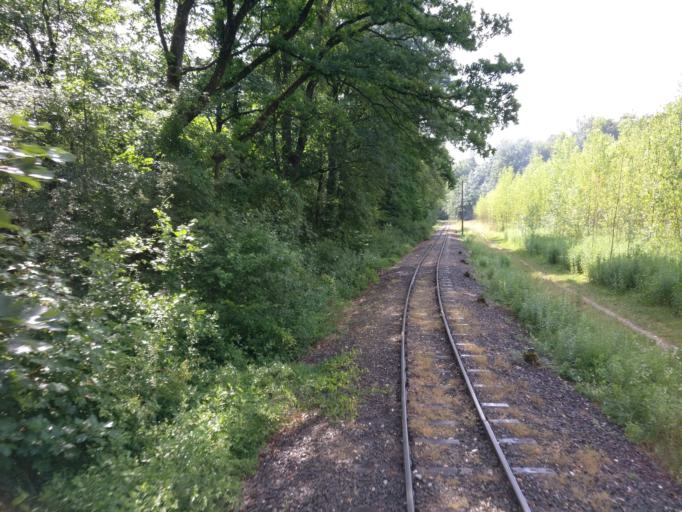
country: AT
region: Upper Austria
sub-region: Politischer Bezirk Steyr-Land
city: Garsten
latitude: 48.0462
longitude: 14.3684
